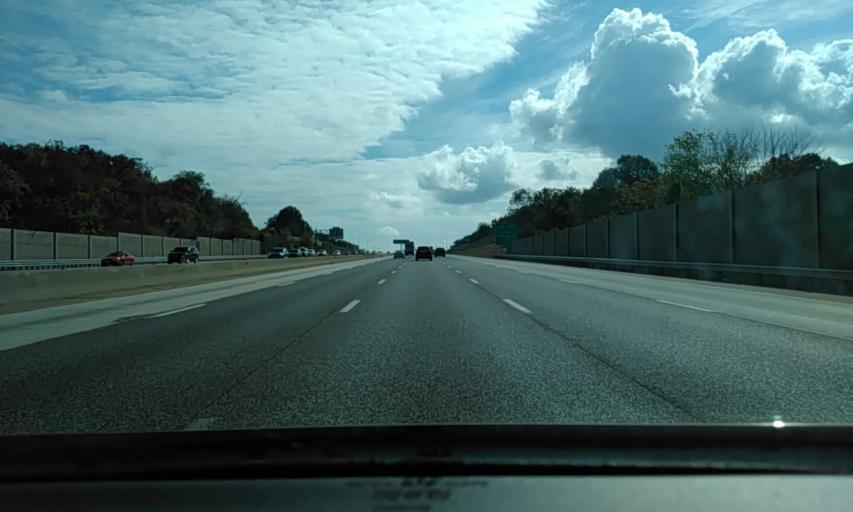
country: US
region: Missouri
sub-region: Saint Louis County
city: Concord
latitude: 38.5105
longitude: -90.3619
